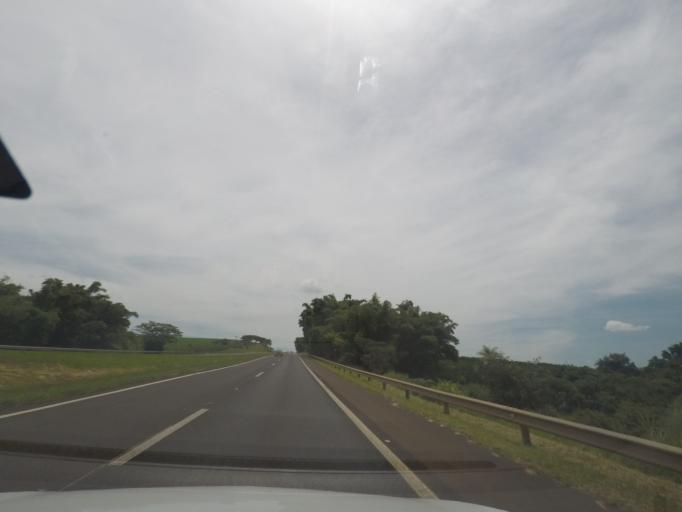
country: BR
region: Sao Paulo
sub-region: Bebedouro
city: Bebedouro
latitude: -21.0282
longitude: -48.4215
